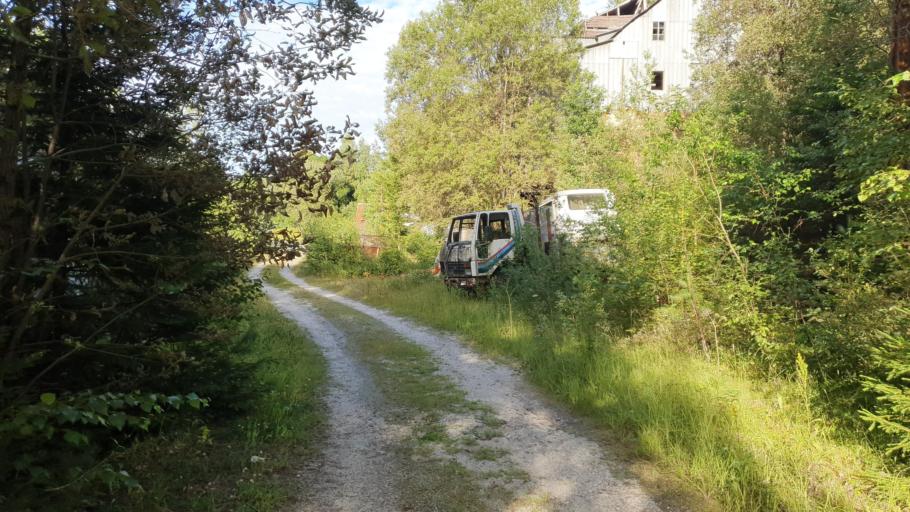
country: SE
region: Vaestra Goetaland
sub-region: Fargelanda Kommun
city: Faergelanda
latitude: 58.5310
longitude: 12.0782
